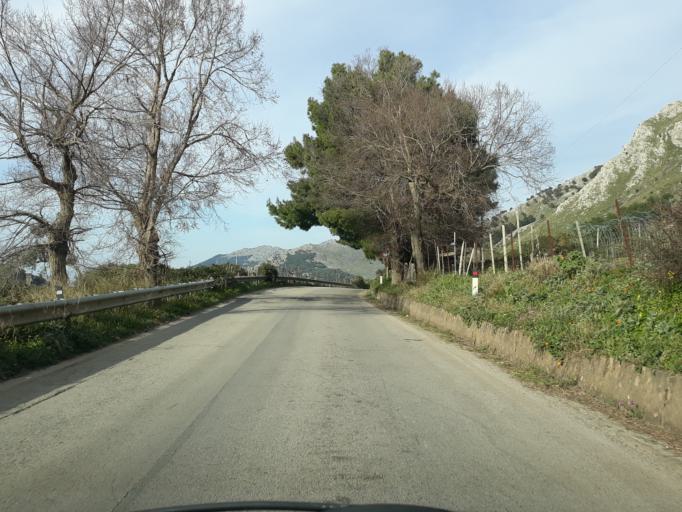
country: IT
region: Sicily
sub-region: Palermo
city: Torretta
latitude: 38.1080
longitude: 13.2357
